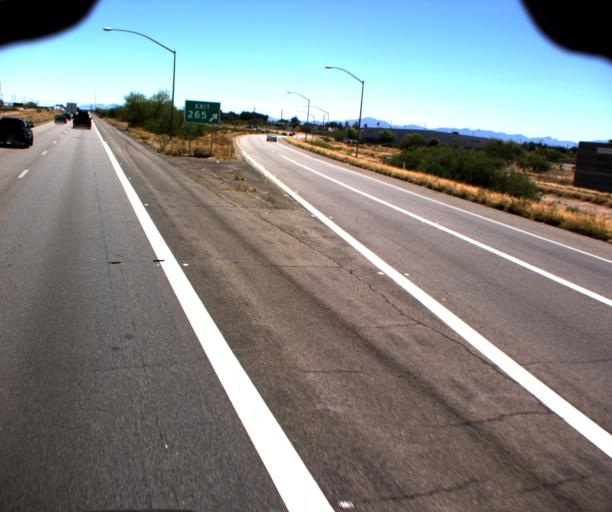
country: US
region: Arizona
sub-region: Pima County
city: Tucson
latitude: 32.1597
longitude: -110.9135
